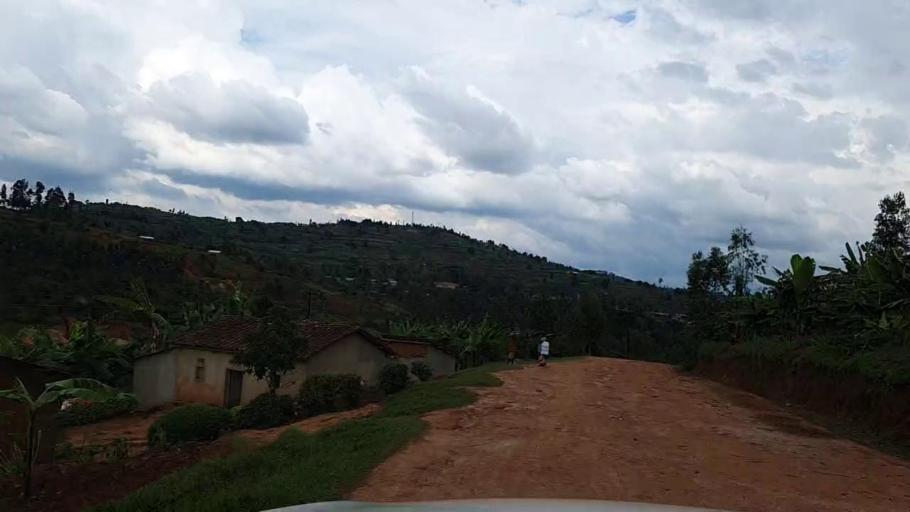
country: RW
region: Southern Province
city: Gikongoro
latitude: -2.4163
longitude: 29.6567
